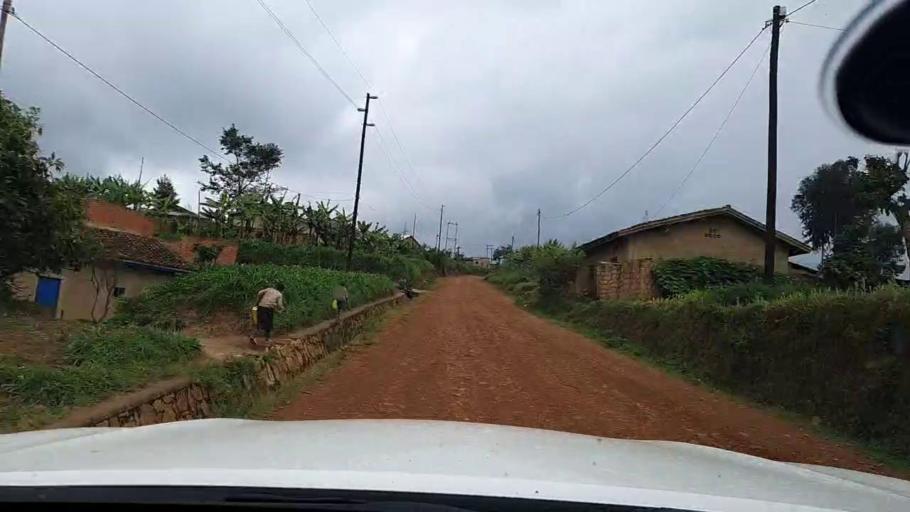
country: RW
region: Western Province
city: Kibuye
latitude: -2.1751
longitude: 29.4424
